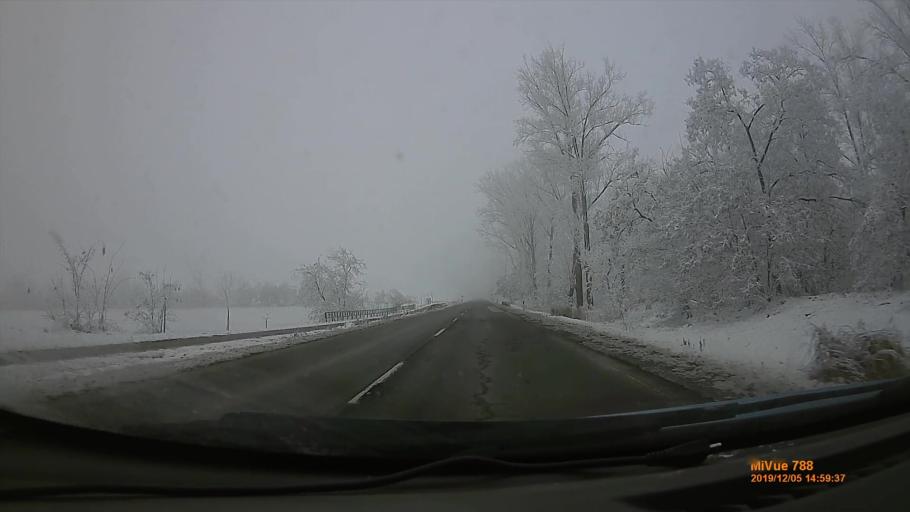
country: HU
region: Szabolcs-Szatmar-Bereg
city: Tiszanagyfalu
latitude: 48.0584
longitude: 21.5543
